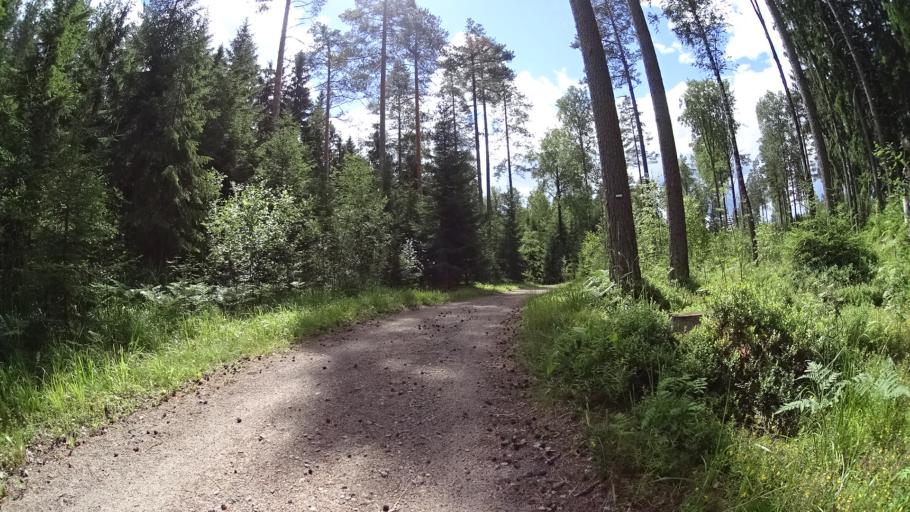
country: FI
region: Uusimaa
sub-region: Helsinki
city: Espoo
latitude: 60.2832
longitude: 24.6108
